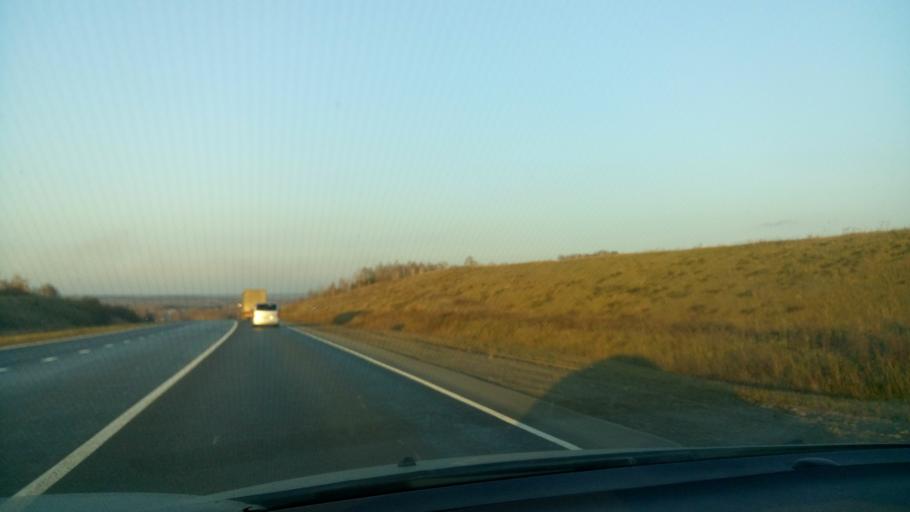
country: RU
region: Sverdlovsk
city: Yelanskiy
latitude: 56.7893
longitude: 62.5077
